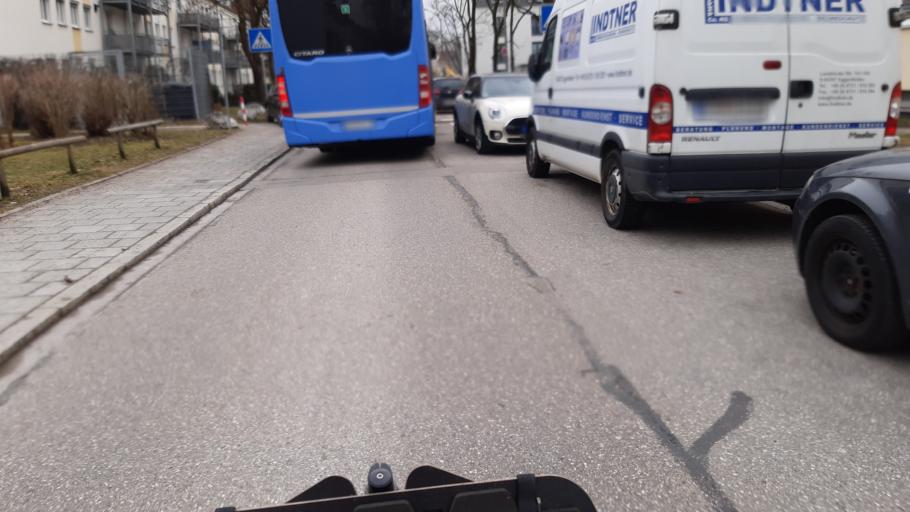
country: DE
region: Bavaria
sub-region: Upper Bavaria
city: Karlsfeld
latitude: 48.2148
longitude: 11.4868
